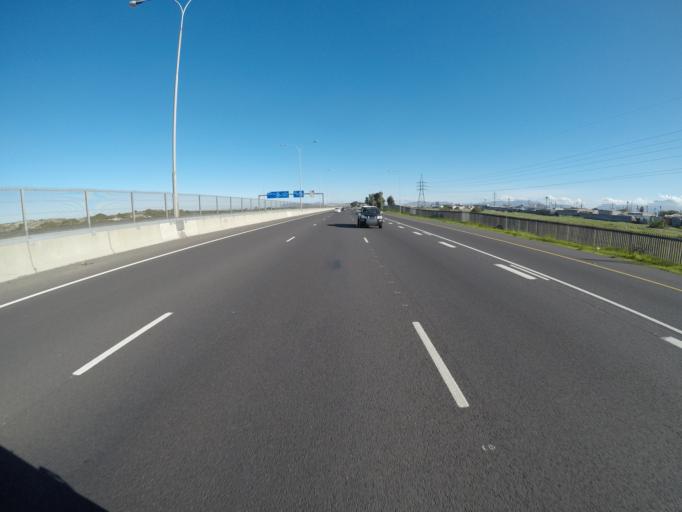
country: ZA
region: Western Cape
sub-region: City of Cape Town
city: Lansdowne
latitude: -33.9935
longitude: 18.6409
